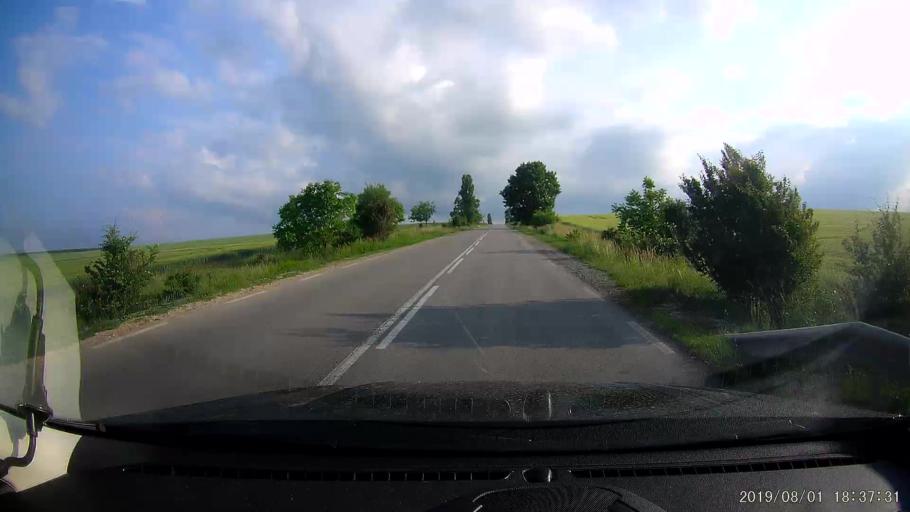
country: BG
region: Shumen
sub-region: Obshtina Khitrino
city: Gara Khitrino
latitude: 43.4193
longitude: 26.9294
